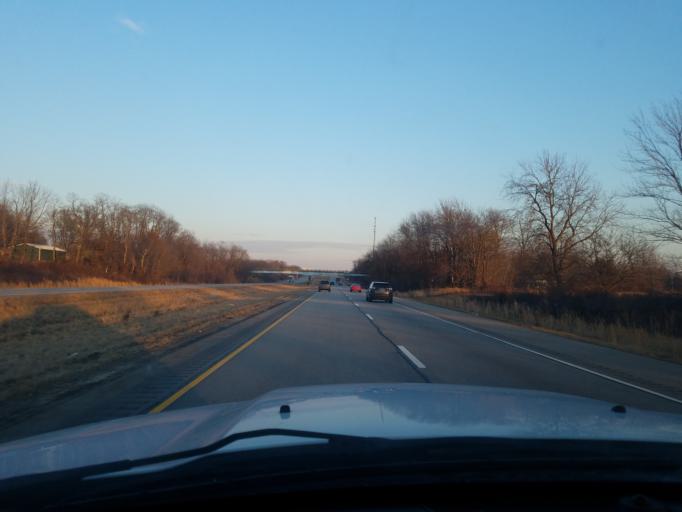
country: US
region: Indiana
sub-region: Gibson County
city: Haubstadt
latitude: 38.1696
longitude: -87.4502
